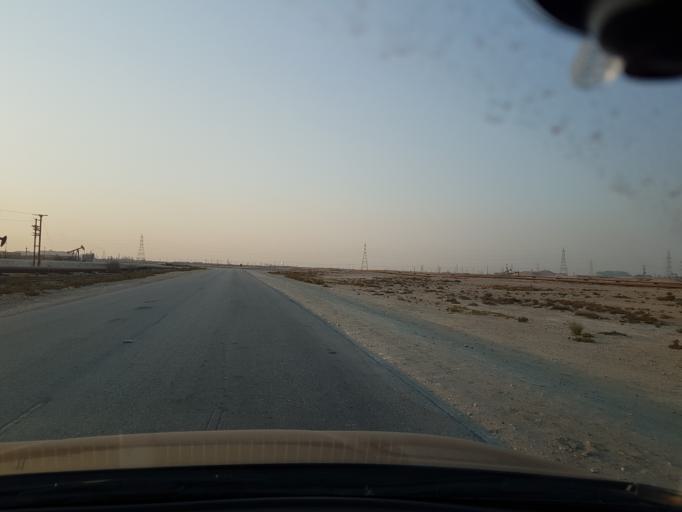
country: BH
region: Central Governorate
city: Dar Kulayb
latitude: 26.0121
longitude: 50.5798
